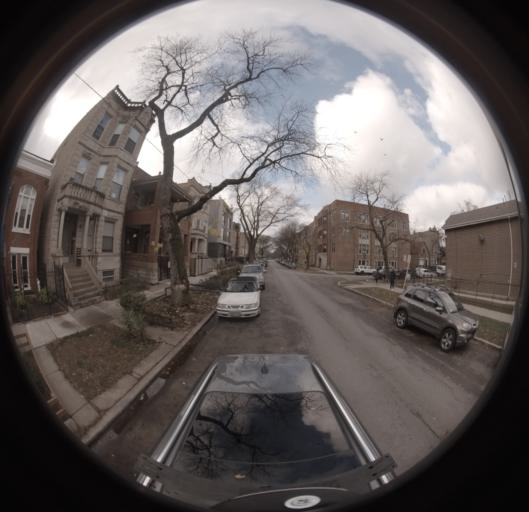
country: US
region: Illinois
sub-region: Cook County
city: Chicago
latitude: 41.9067
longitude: -87.6940
